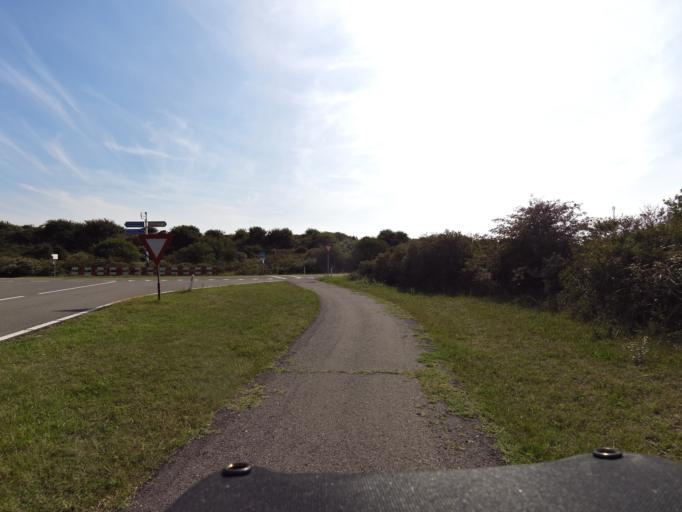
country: NL
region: Zeeland
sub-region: Schouwen-Duiveland
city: Scharendijke
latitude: 51.7854
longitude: 3.8746
